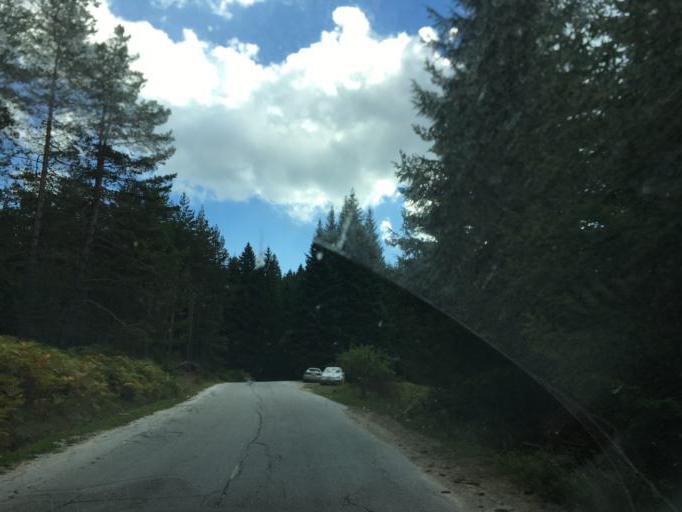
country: BG
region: Pazardzhik
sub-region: Obshtina Batak
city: Batak
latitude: 41.9113
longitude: 24.2888
